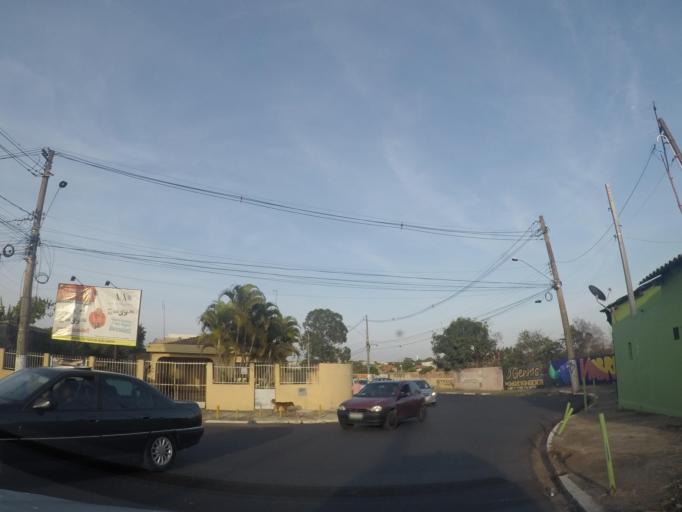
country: BR
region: Sao Paulo
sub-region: Hortolandia
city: Hortolandia
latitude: -22.8486
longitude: -47.1801
